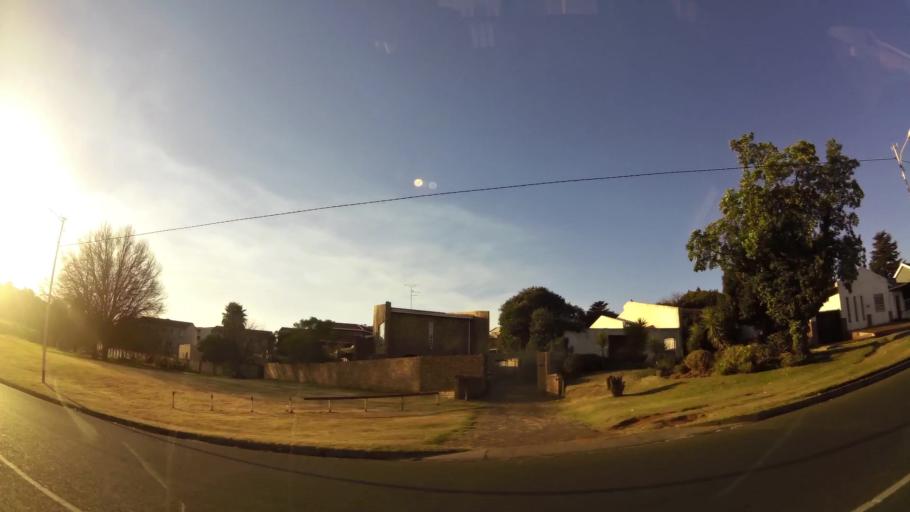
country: ZA
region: Gauteng
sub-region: City of Johannesburg Metropolitan Municipality
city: Roodepoort
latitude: -26.1645
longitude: 27.8858
